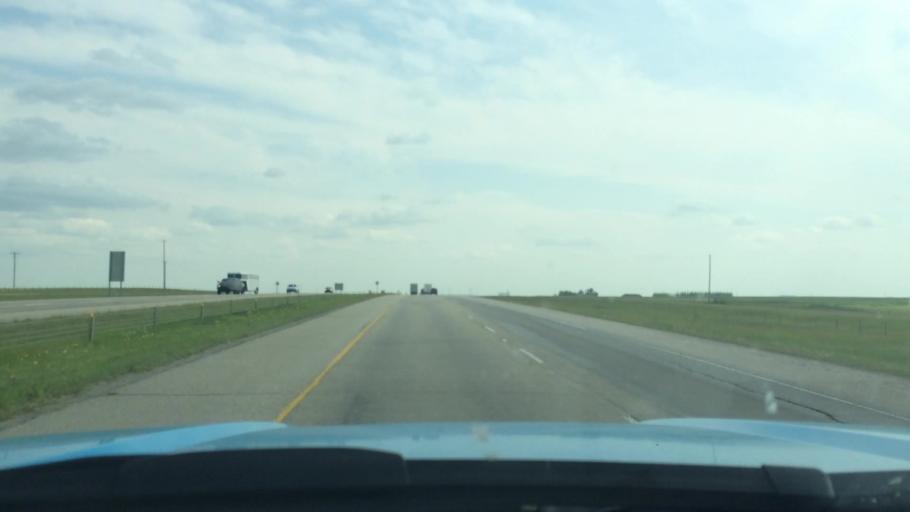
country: CA
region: Alberta
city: Carstairs
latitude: 51.5420
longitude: -114.0253
